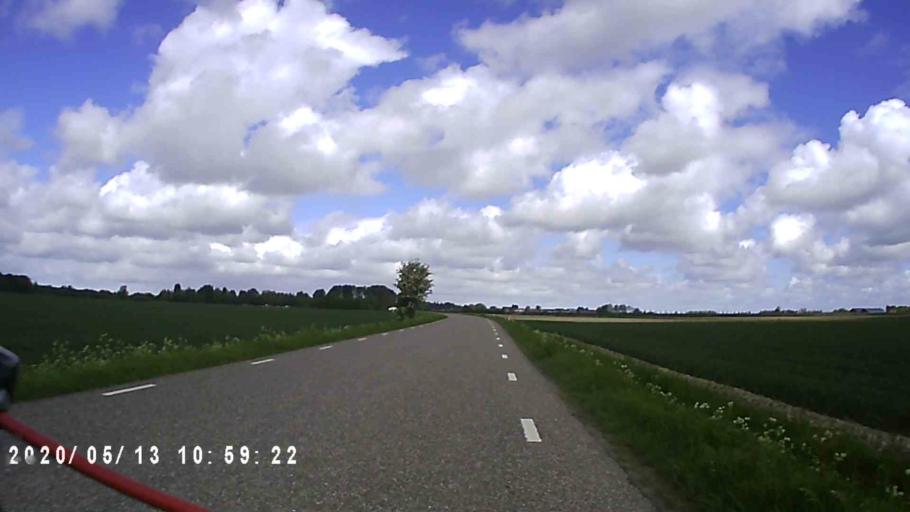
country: NL
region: Groningen
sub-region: Gemeente Zuidhorn
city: Grijpskerk
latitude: 53.2782
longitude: 6.3330
